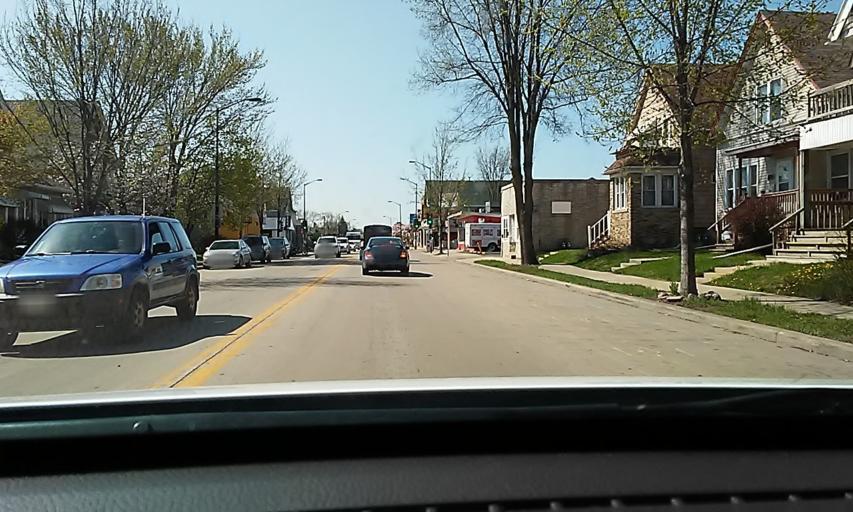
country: US
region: Wisconsin
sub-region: Milwaukee County
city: West Milwaukee
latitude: 43.0110
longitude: -87.9874
